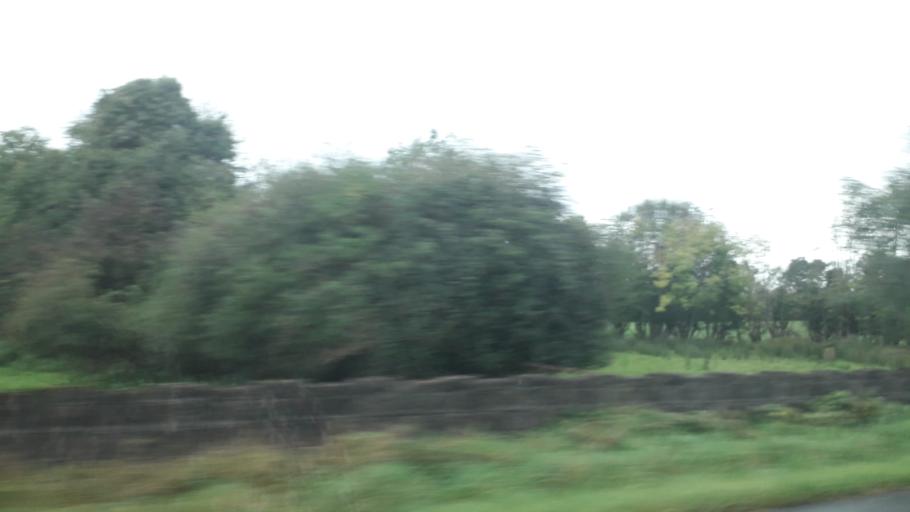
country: IE
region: Leinster
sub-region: An Longfort
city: Longford
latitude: 53.7253
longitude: -7.8496
